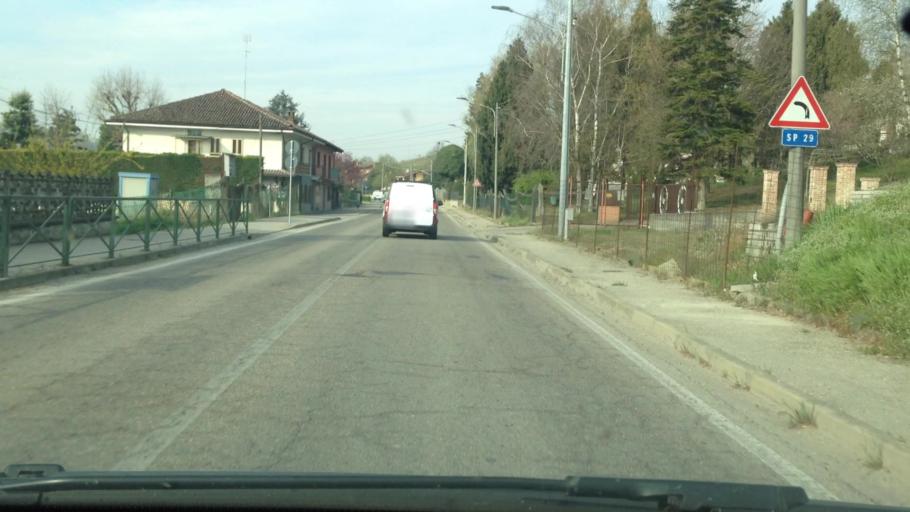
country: IT
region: Piedmont
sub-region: Provincia di Cuneo
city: Canale
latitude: 44.8027
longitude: 8.0193
